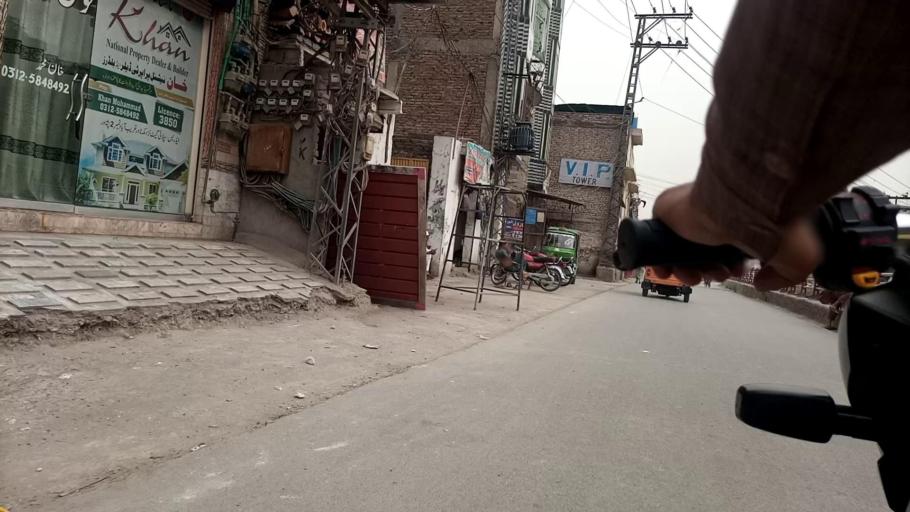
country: PK
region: Khyber Pakhtunkhwa
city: Peshawar
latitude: 34.0200
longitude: 71.5928
